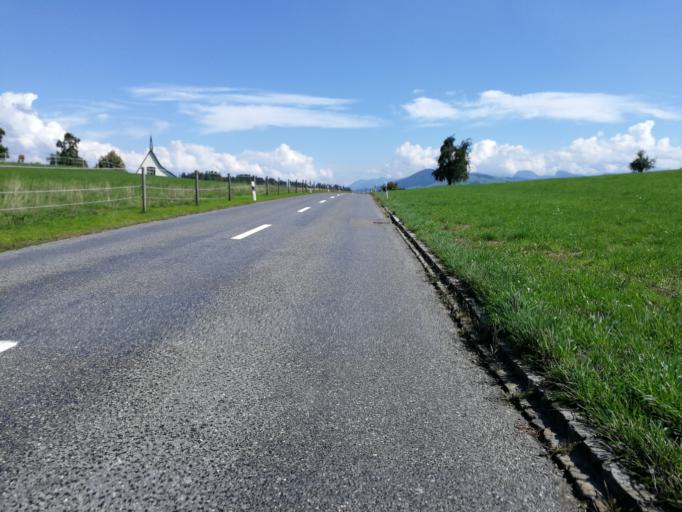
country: CH
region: Zurich
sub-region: Bezirk Horgen
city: Waedenswil / Untermosen-Fuhr
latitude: 47.2111
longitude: 8.6524
